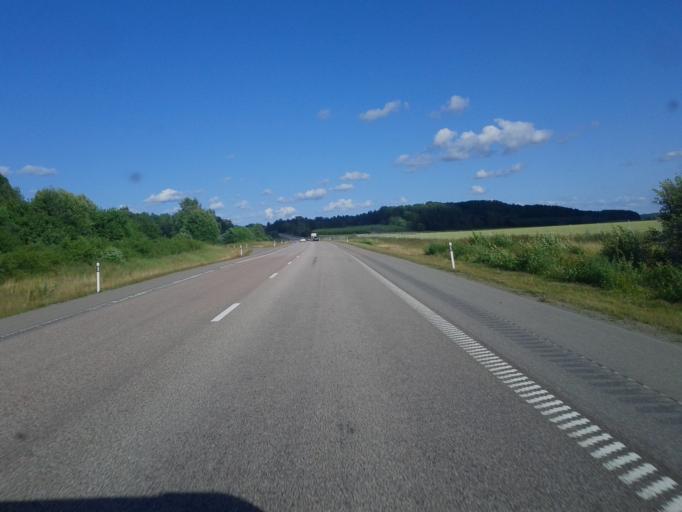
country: SE
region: Uppsala
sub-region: Enkopings Kommun
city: Grillby
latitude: 59.6337
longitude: 17.2883
